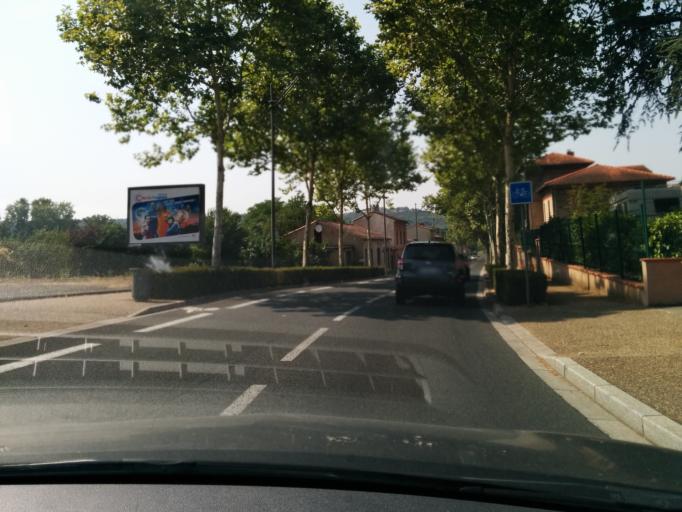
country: FR
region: Midi-Pyrenees
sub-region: Departement du Tarn
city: Albi
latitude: 43.9427
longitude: 2.1356
